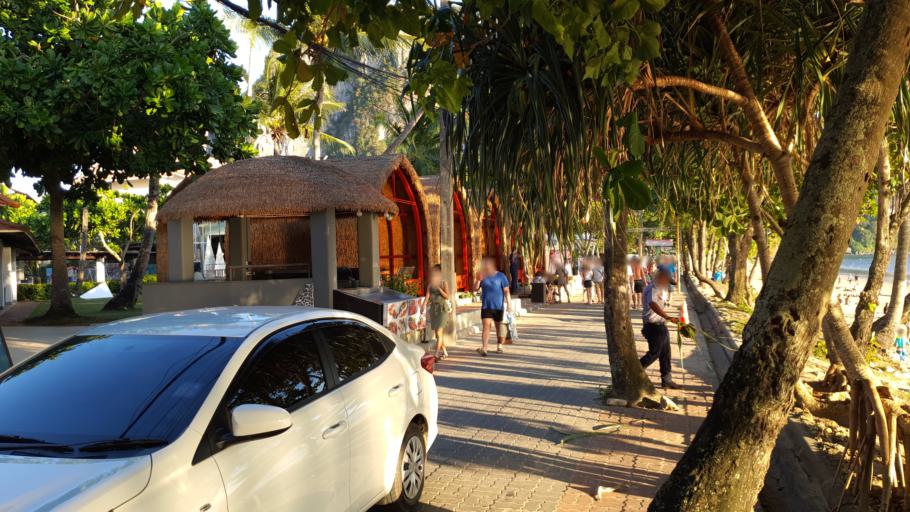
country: TH
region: Phangnga
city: Ban Ao Nang
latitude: 8.0307
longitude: 98.8226
